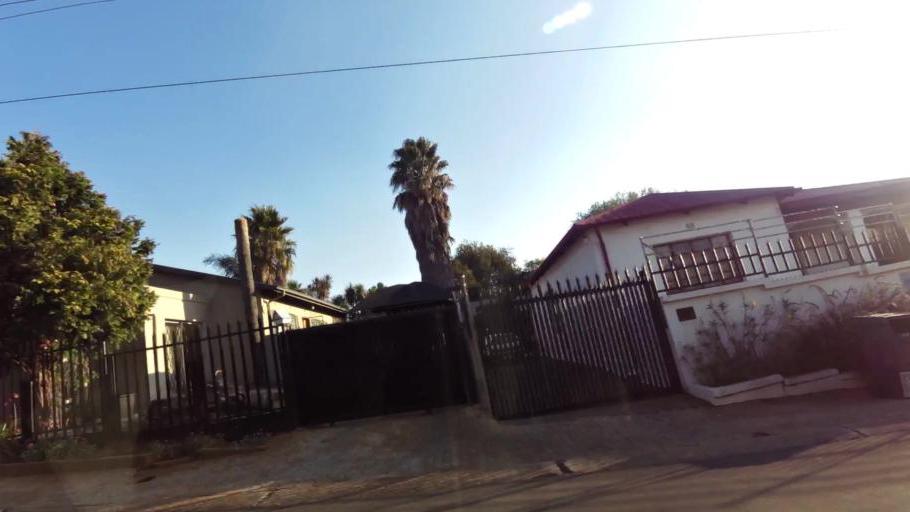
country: ZA
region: Gauteng
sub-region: City of Johannesburg Metropolitan Municipality
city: Johannesburg
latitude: -26.1643
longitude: 27.9789
